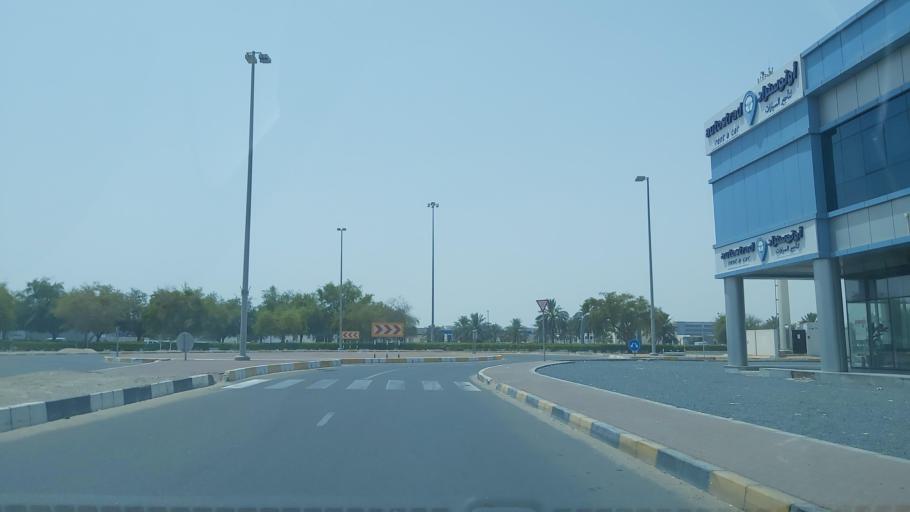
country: AE
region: Abu Dhabi
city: Abu Dhabi
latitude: 24.3749
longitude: 54.5203
